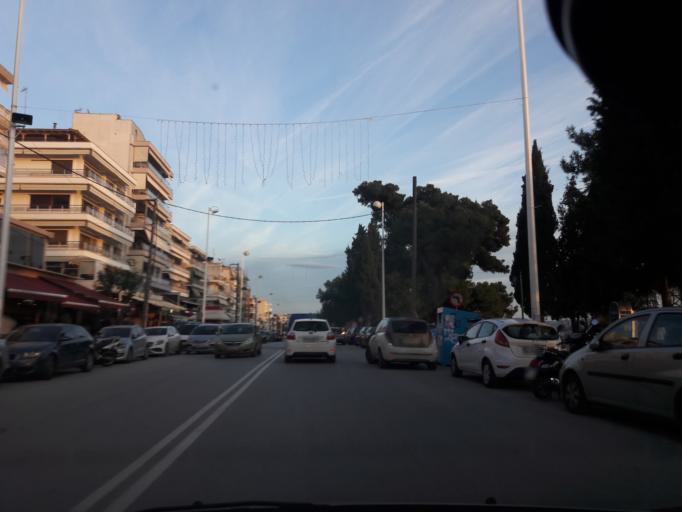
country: GR
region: Central Macedonia
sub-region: Nomos Thessalonikis
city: Kalamaria
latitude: 40.5752
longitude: 22.9481
